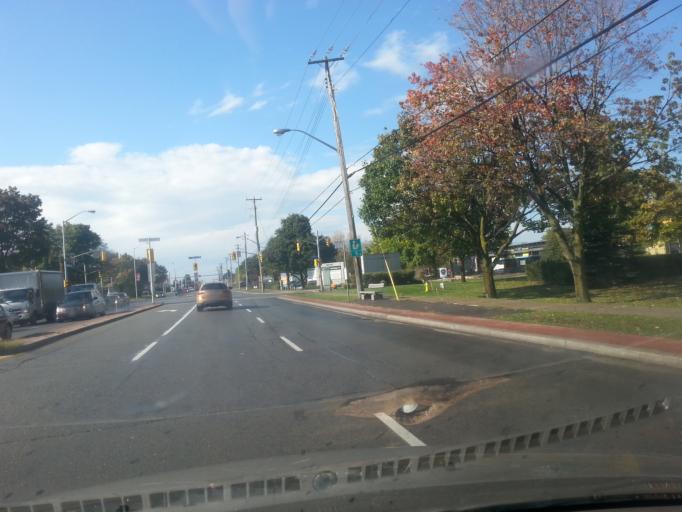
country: CA
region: Ontario
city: Bells Corners
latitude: 45.3267
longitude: -75.8222
